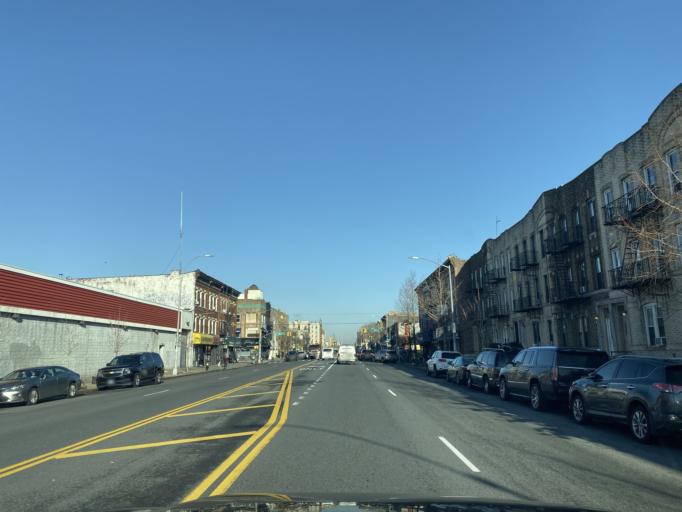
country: US
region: New York
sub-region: Kings County
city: Bensonhurst
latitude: 40.6116
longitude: -73.9626
